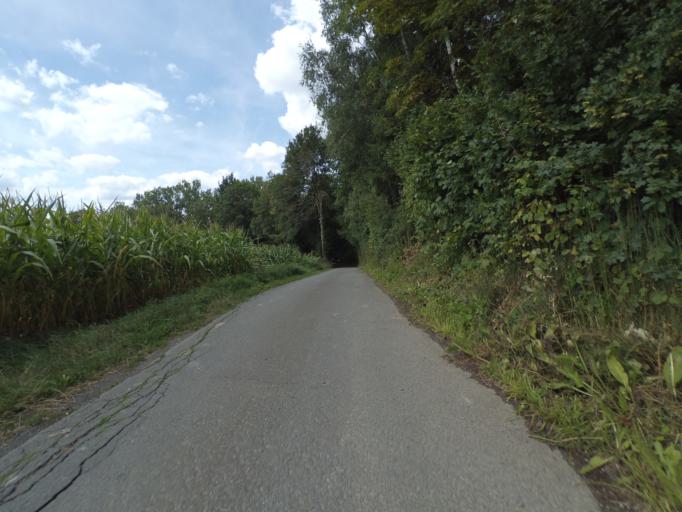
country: BE
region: Wallonia
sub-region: Province du Hainaut
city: Ellezelles
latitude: 50.8156
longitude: 3.6836
